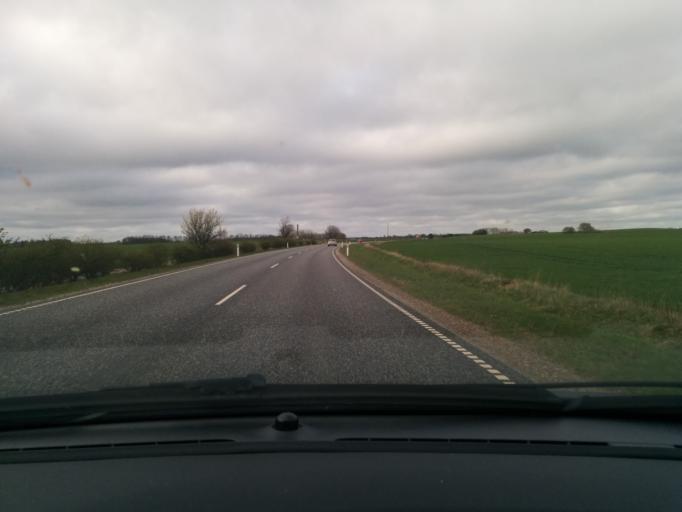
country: DK
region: Central Jutland
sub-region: Favrskov Kommune
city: Hammel
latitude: 56.2236
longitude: 9.8514
